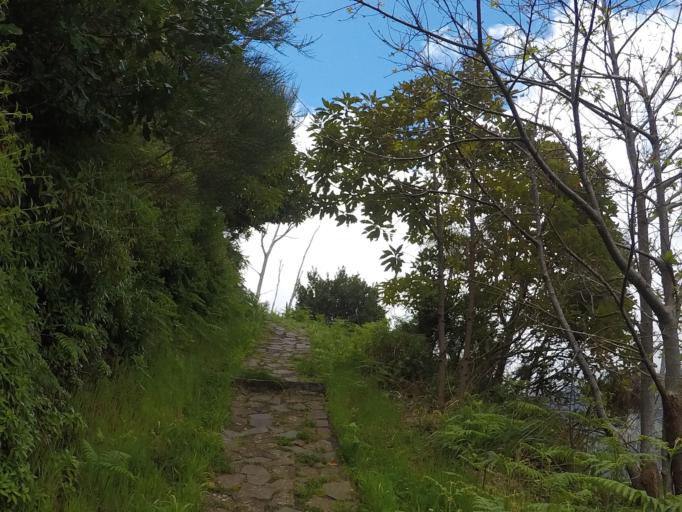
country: PT
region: Madeira
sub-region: Camara de Lobos
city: Curral das Freiras
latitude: 32.7415
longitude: -17.0062
